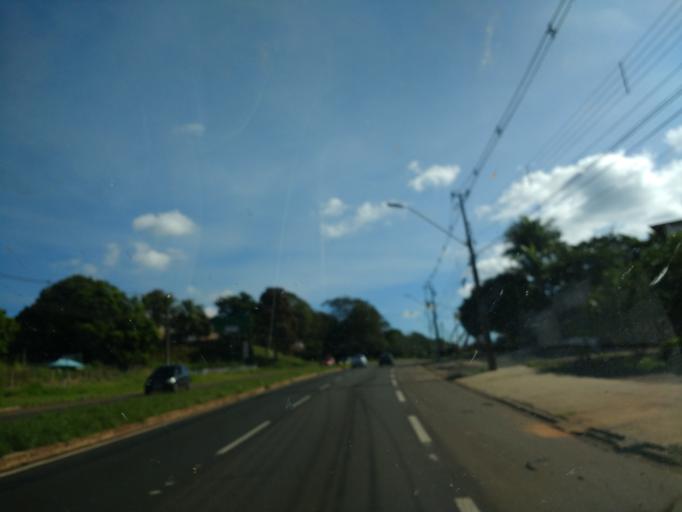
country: BR
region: Parana
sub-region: Maringa
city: Maringa
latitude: -23.4190
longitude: -51.9642
